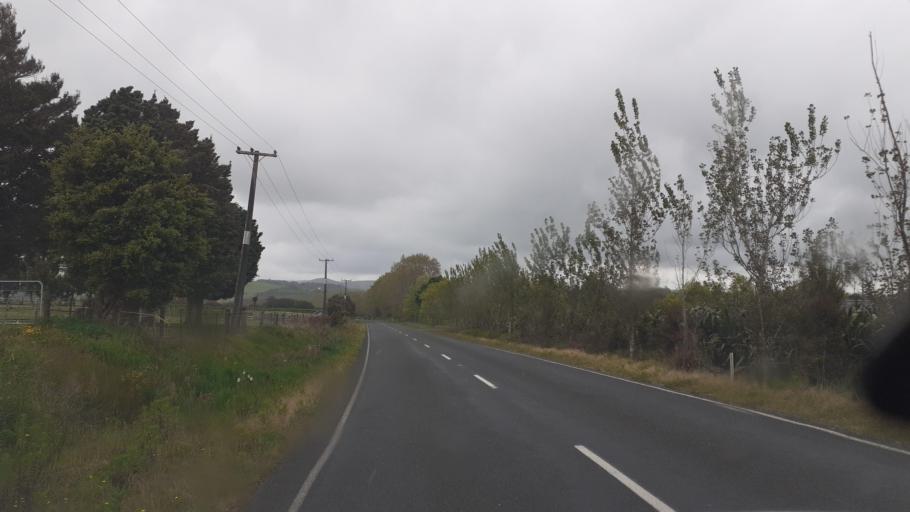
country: NZ
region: Northland
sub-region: Far North District
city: Waimate North
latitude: -35.2758
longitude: 173.8301
